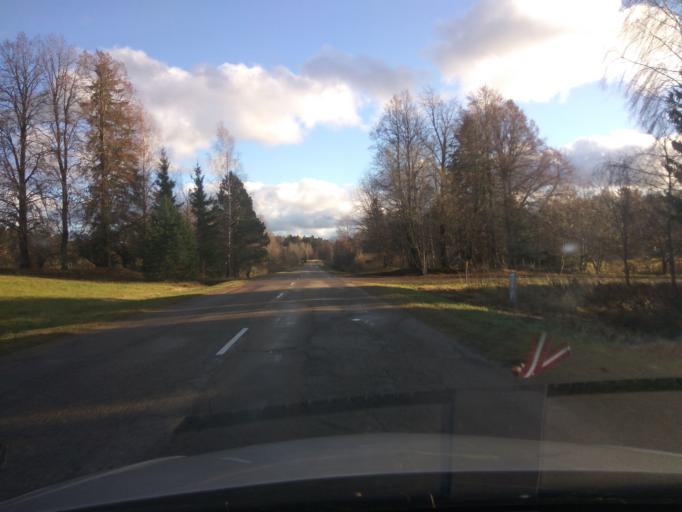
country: LV
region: Aizpute
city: Aizpute
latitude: 56.7458
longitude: 21.5776
